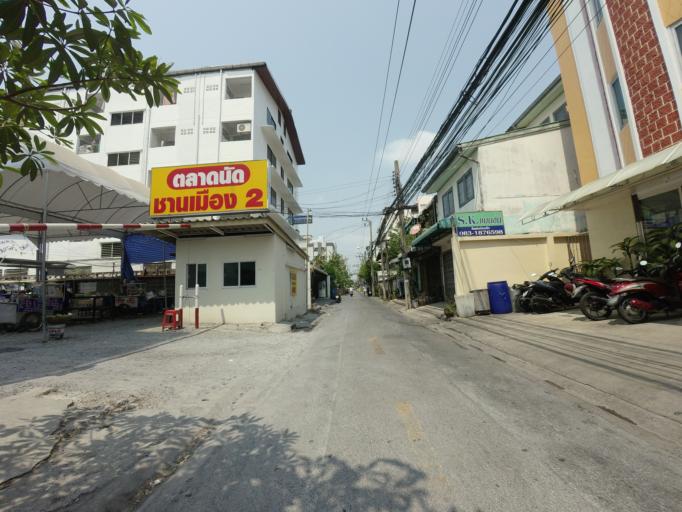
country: TH
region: Bangkok
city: Din Daeng
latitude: 13.7680
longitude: 100.5656
